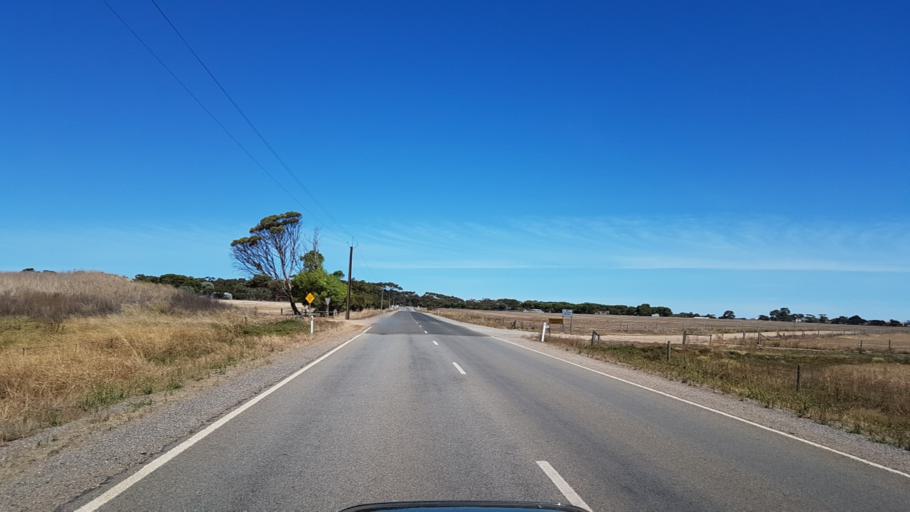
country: AU
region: South Australia
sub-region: Yorke Peninsula
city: Maitland
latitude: -34.3628
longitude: 137.6675
